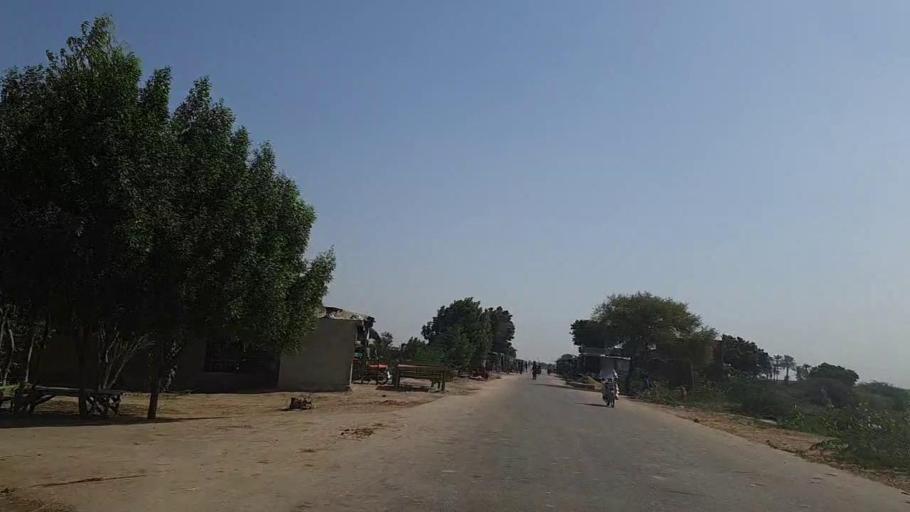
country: PK
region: Sindh
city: Mirpur Batoro
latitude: 24.7599
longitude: 68.2225
